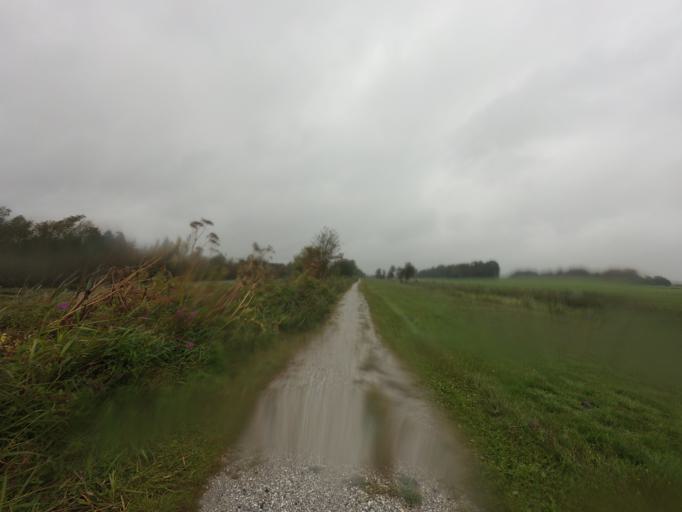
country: NL
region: Friesland
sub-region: Gemeente Smallingerland
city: Oudega
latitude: 53.0973
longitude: 5.9818
